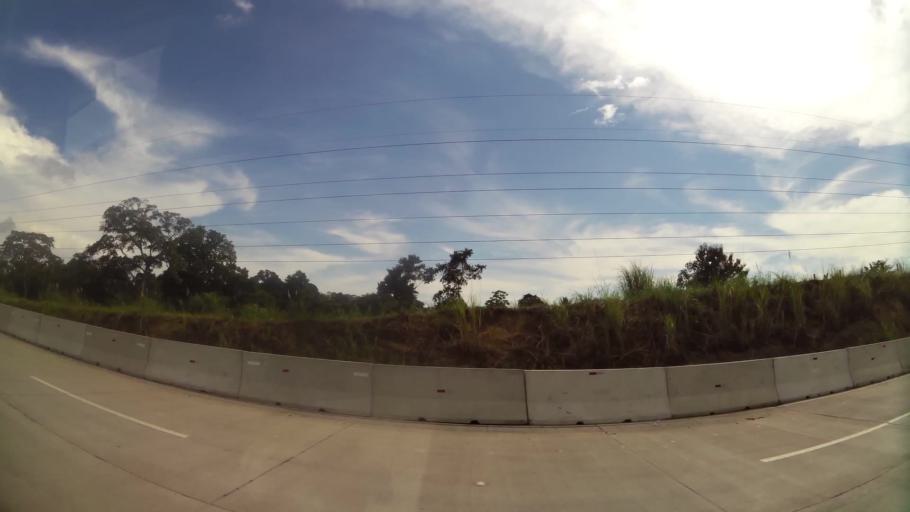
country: PA
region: Panama
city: Tocumen
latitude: 9.0914
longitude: -79.4284
